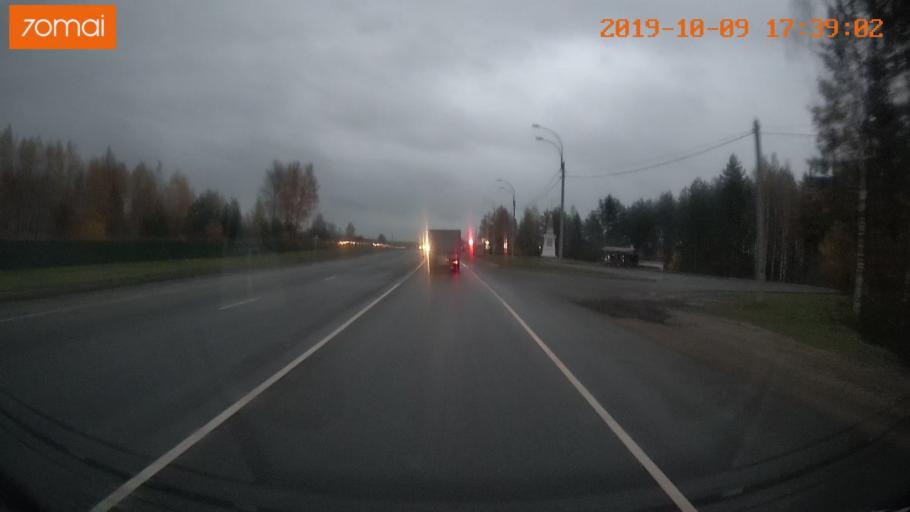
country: RU
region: Ivanovo
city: Bogorodskoye
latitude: 57.0644
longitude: 40.9537
